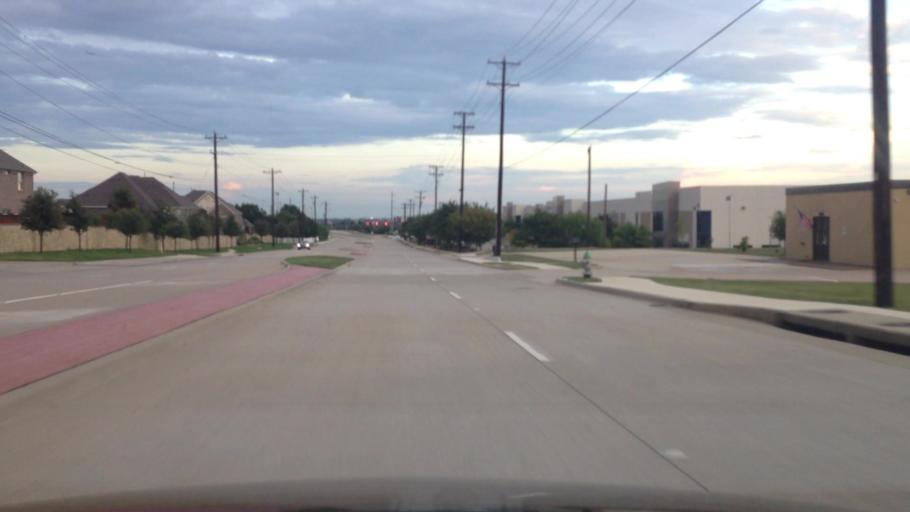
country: US
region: Texas
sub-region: Denton County
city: Flower Mound
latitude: 32.9986
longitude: -97.0503
